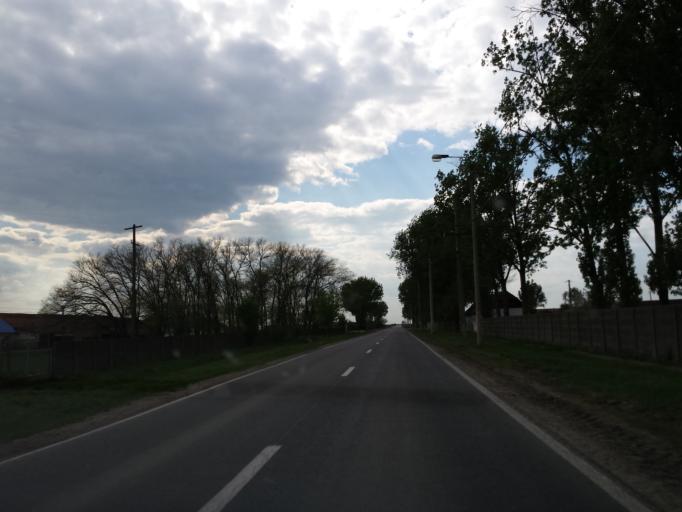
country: RO
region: Timis
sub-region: Comuna Cenad
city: Cenad
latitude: 46.1292
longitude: 20.5551
